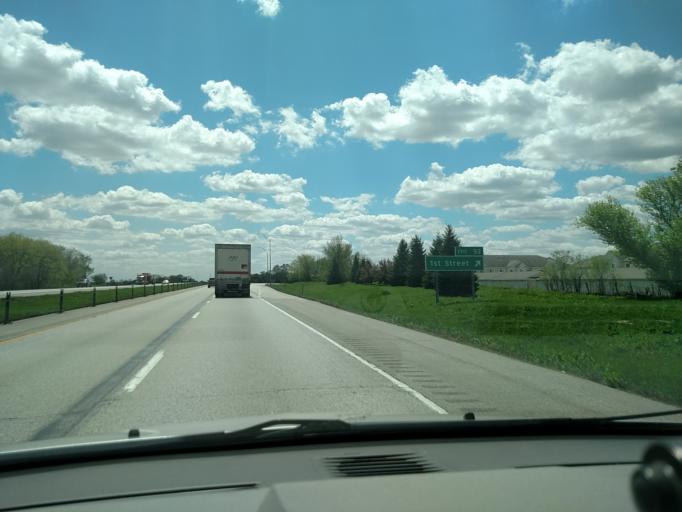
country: US
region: Iowa
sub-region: Polk County
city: Ankeny
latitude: 41.7375
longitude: -93.5779
